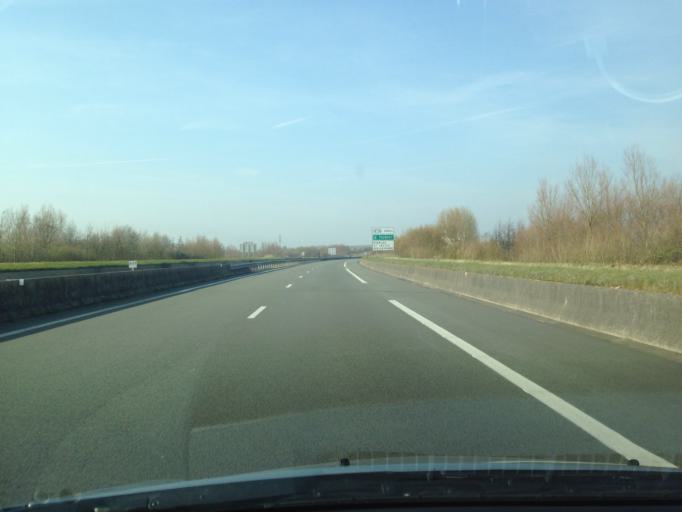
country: FR
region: Nord-Pas-de-Calais
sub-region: Departement du Pas-de-Calais
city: Saint-Josse
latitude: 50.4962
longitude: 1.6803
